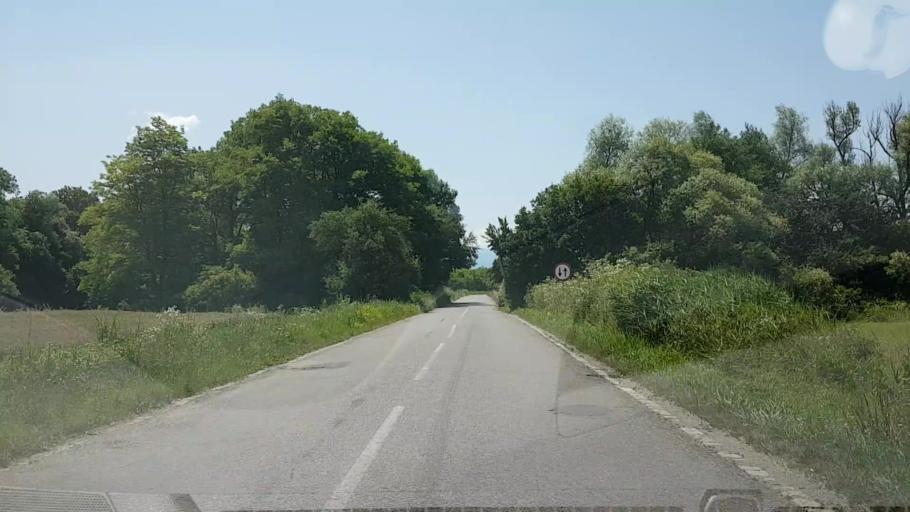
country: RO
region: Brasov
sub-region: Comuna Cincu
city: Cincu
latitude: 45.8875
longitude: 24.8128
